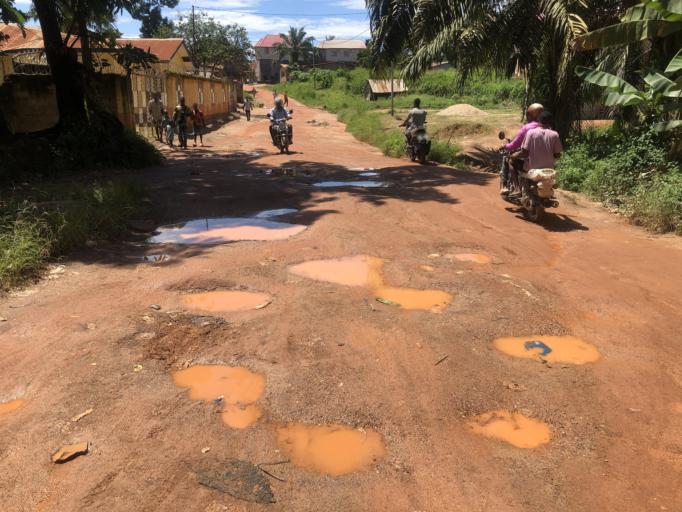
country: SL
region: Eastern Province
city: Koidu
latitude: 8.6431
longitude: -10.9625
